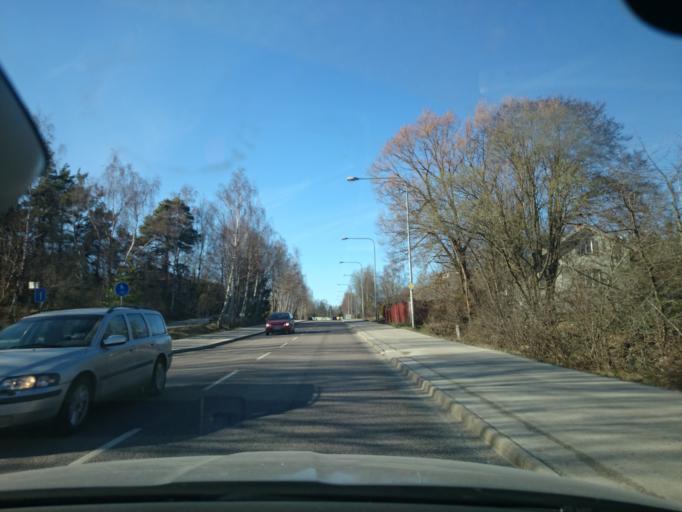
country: SE
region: Stockholm
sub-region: Huddinge Kommun
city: Huddinge
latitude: 59.2619
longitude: 17.9722
